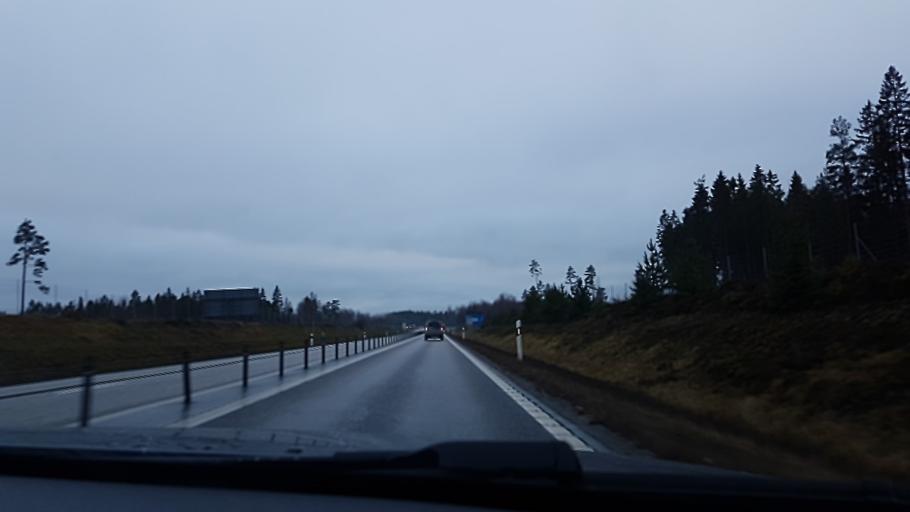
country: SE
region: Kronoberg
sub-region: Ljungby Kommun
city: Lagan
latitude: 56.9673
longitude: 14.0136
